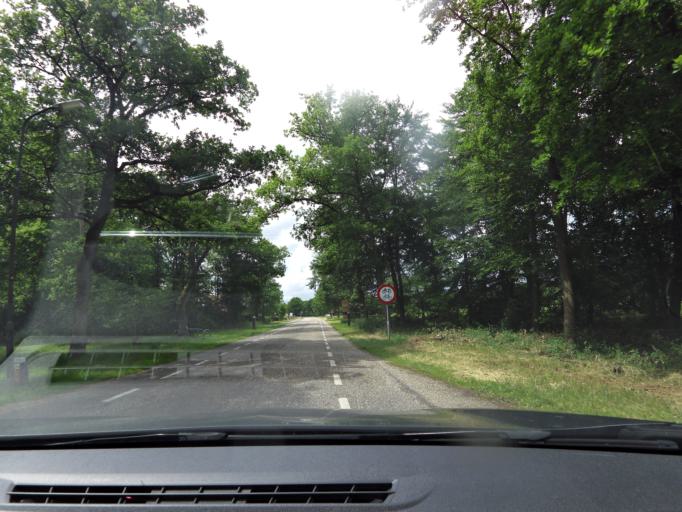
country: NL
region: Gelderland
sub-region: Gemeente Apeldoorn
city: Uddel
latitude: 52.2560
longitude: 5.7955
